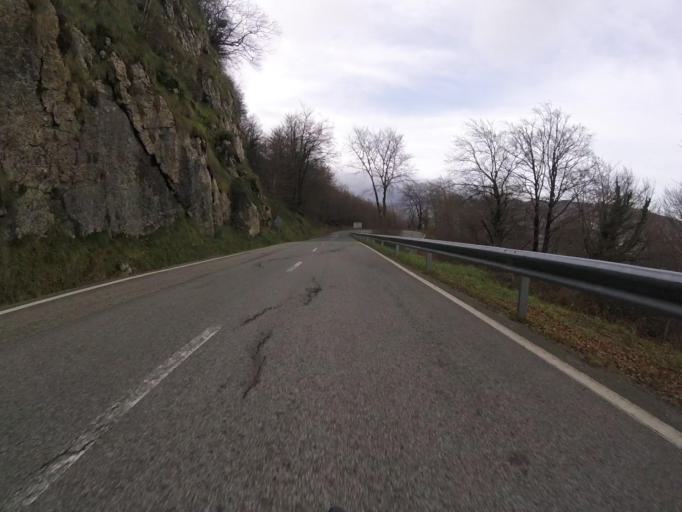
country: ES
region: Navarre
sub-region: Provincia de Navarra
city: Olazagutia
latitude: 42.8606
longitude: -2.1883
